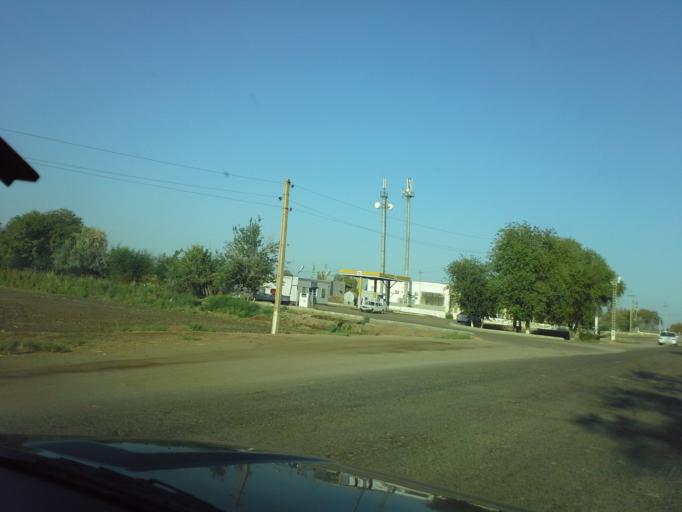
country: UZ
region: Karakalpakstan
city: Khujayli
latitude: 42.2199
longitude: 59.4915
